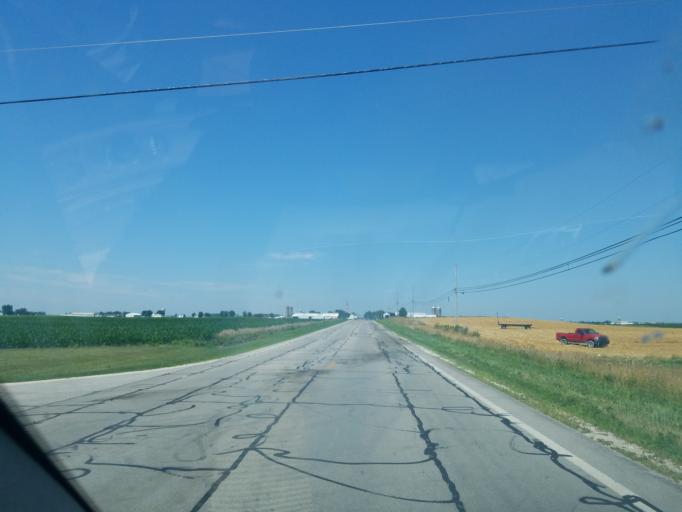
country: US
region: Ohio
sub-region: Auglaize County
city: New Bremen
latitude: 40.4077
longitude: -84.5030
